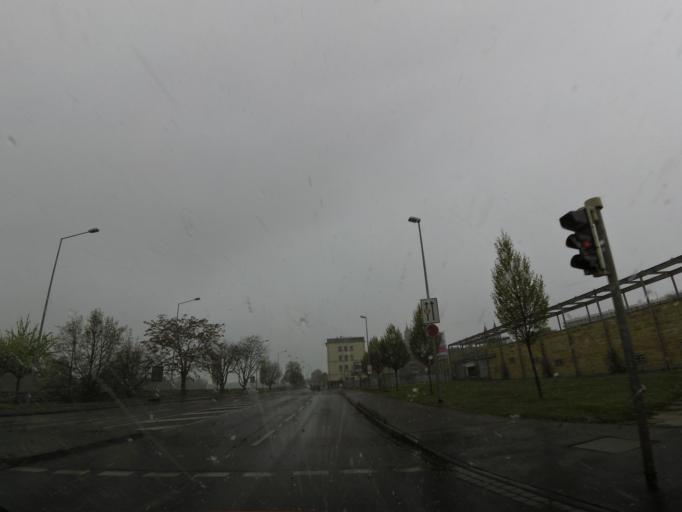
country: DE
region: Saxony-Anhalt
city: Magdeburg
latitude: 52.1288
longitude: 11.6418
